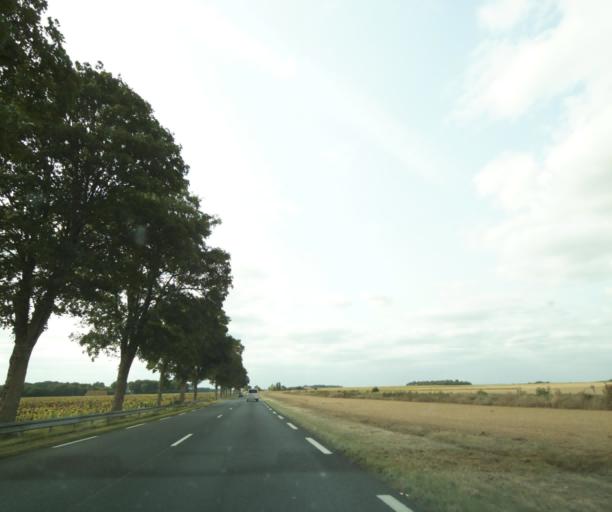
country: FR
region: Centre
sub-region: Departement d'Indre-et-Loire
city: Truyes
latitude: 47.2388
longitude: 0.8652
